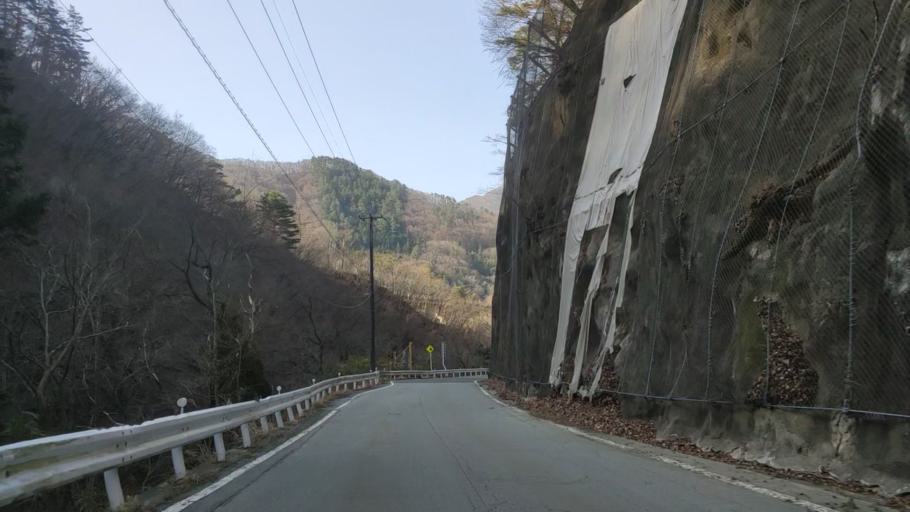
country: JP
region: Yamanashi
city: Fujikawaguchiko
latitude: 35.5329
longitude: 138.6226
